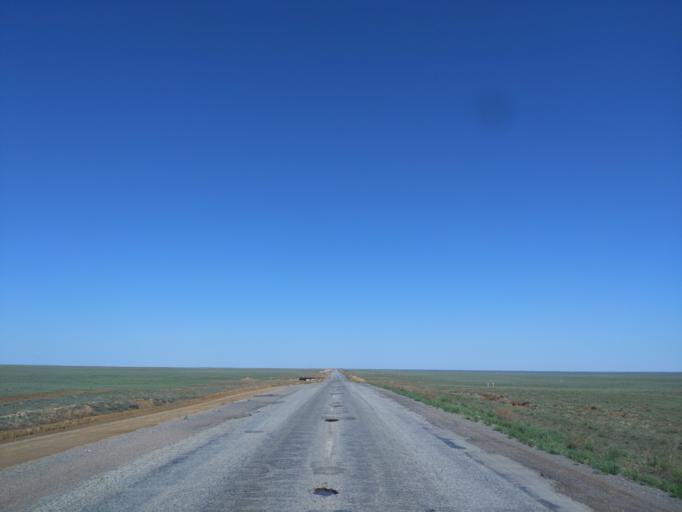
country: KZ
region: Almaty Oblysy
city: Bakanas
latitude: 44.2730
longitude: 75.6240
